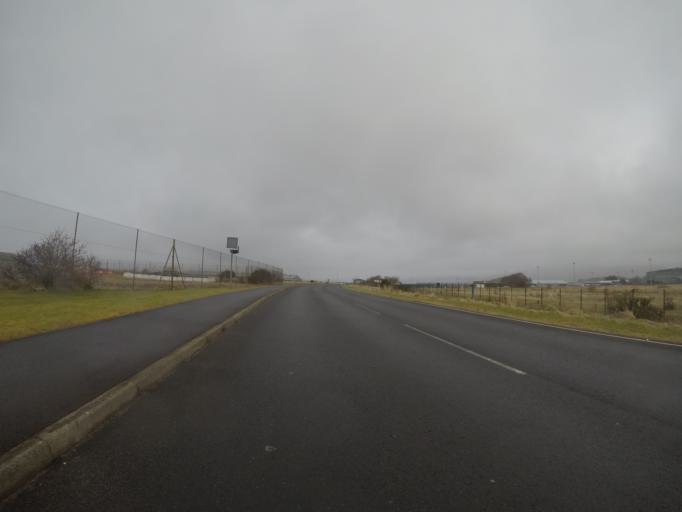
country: GB
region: Scotland
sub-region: North Ayrshire
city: Millport
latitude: 55.7212
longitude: -4.8999
